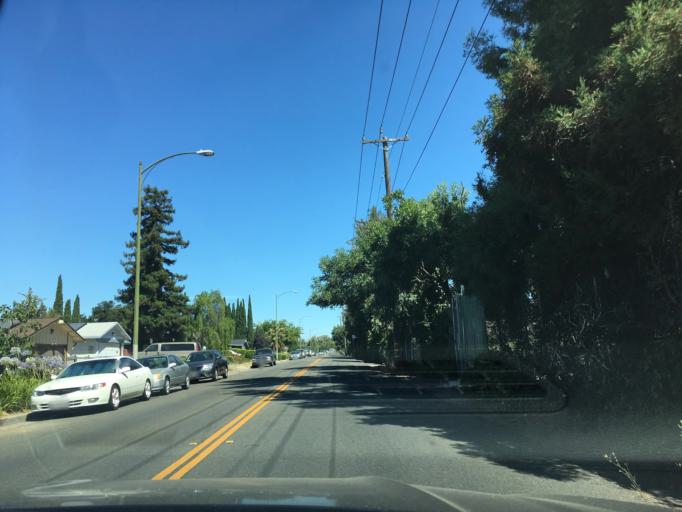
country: US
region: California
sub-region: Santa Clara County
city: East Foothills
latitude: 37.3844
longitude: -121.8286
